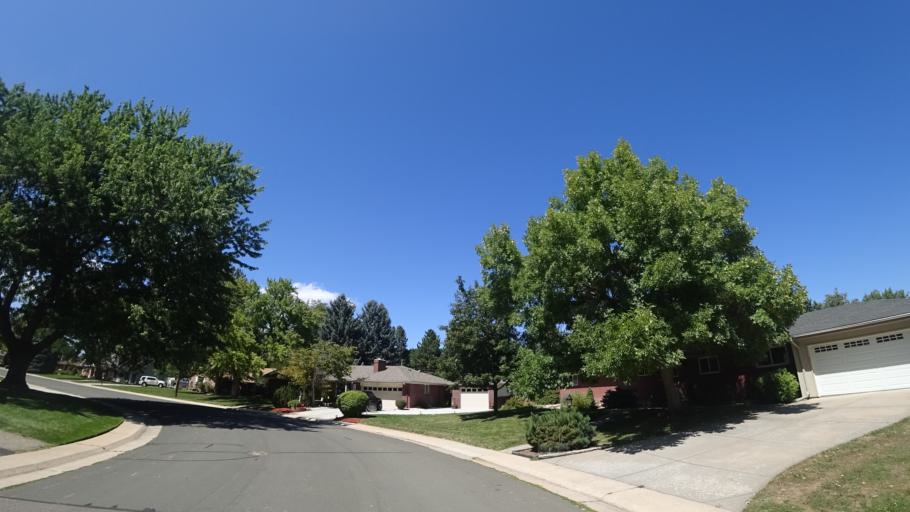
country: US
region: Colorado
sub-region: Arapahoe County
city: Greenwood Village
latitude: 39.6059
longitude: -104.9770
